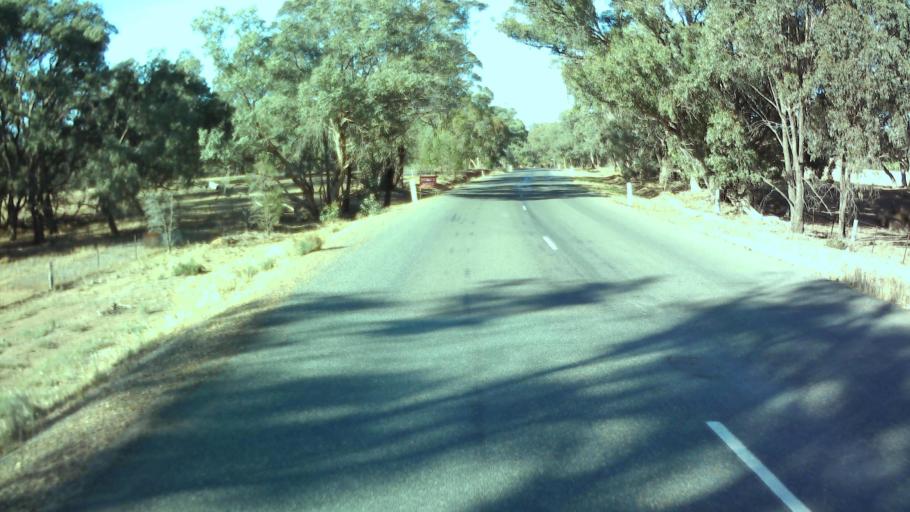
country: AU
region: New South Wales
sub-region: Weddin
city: Grenfell
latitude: -33.9890
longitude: 148.1392
